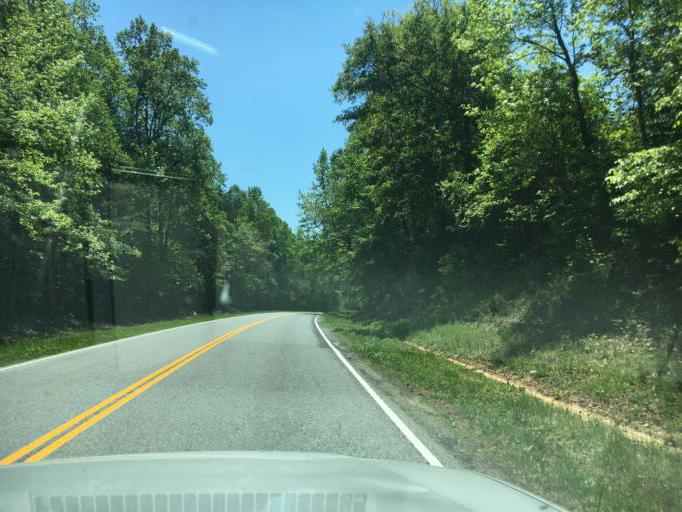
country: US
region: South Carolina
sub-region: Cherokee County
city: Blacksburg
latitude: 35.1295
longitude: -81.5832
